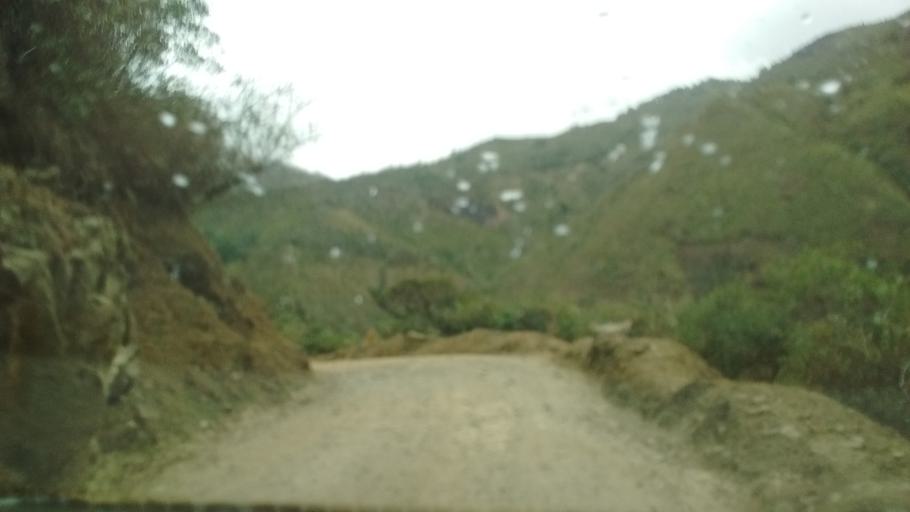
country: CO
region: Cauca
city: La Vega
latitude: 2.0309
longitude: -76.7991
